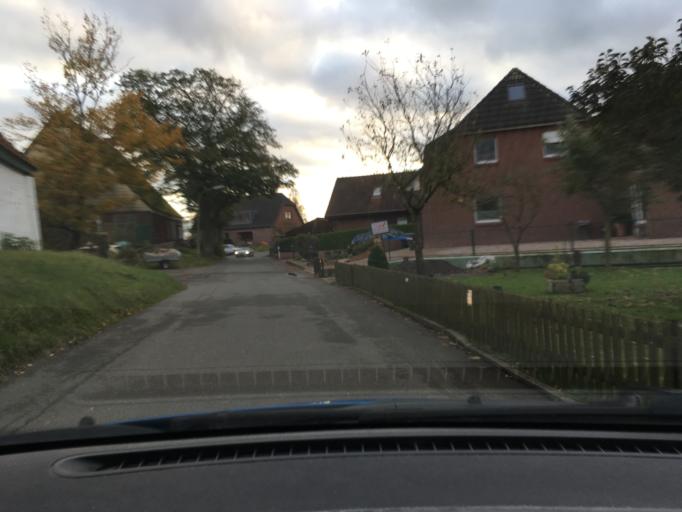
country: DE
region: Hamburg
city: Harburg
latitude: 53.4605
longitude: 10.0457
